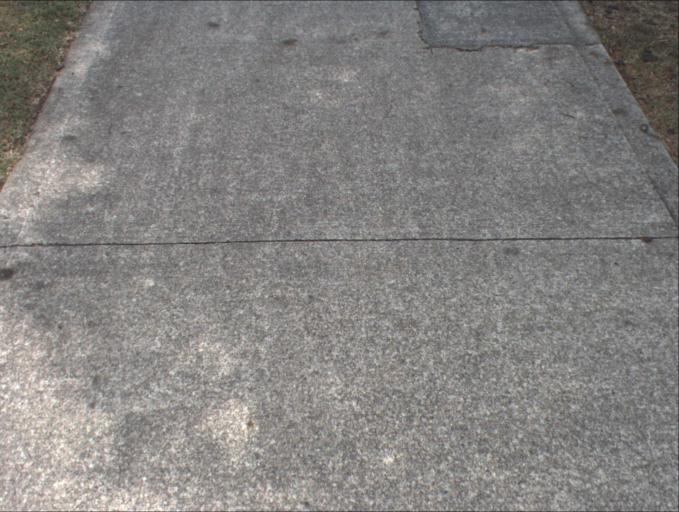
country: AU
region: Queensland
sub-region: Logan
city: Windaroo
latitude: -27.7286
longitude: 153.2080
